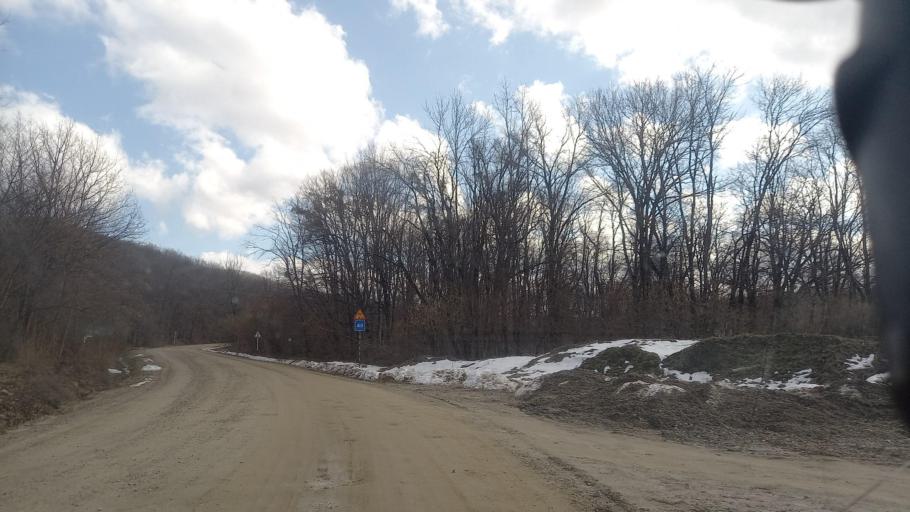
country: RU
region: Krasnodarskiy
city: Smolenskaya
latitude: 44.6209
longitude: 38.7462
